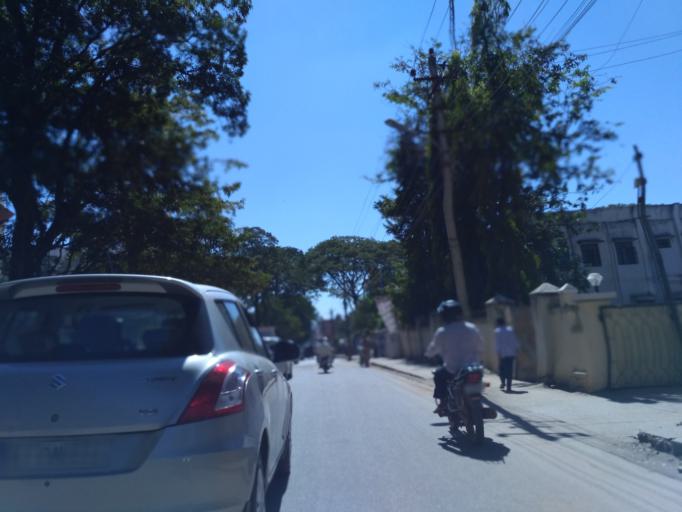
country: IN
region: Karnataka
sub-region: Hassan
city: Hassan
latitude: 13.0062
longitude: 76.1022
